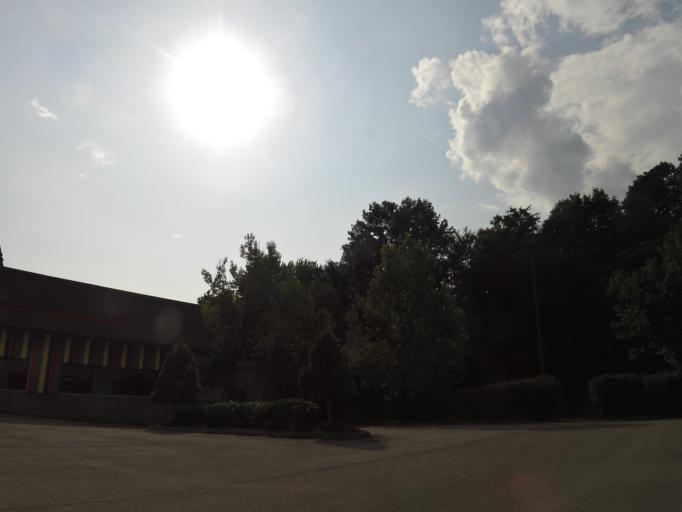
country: US
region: Tennessee
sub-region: Knox County
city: Knoxville
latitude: 36.0325
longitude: -83.8803
